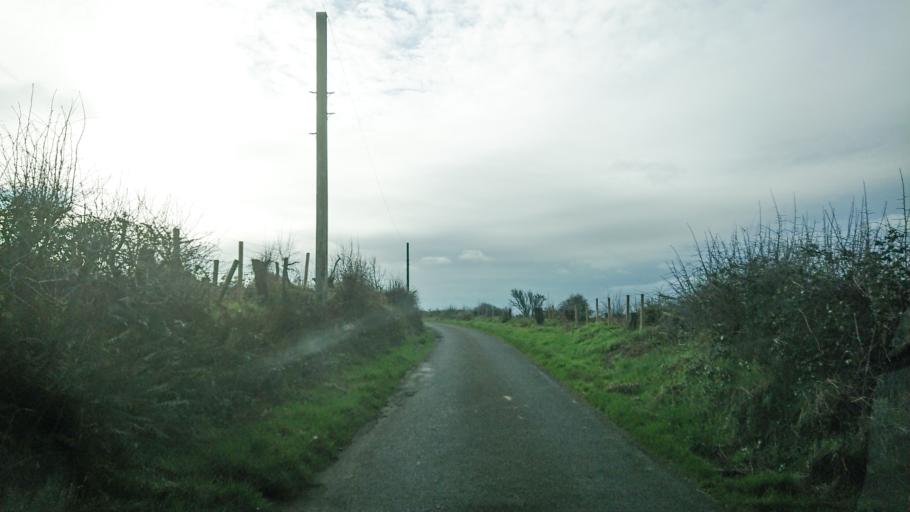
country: IE
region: Munster
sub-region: Waterford
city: Tra Mhor
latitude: 52.1494
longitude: -7.1925
